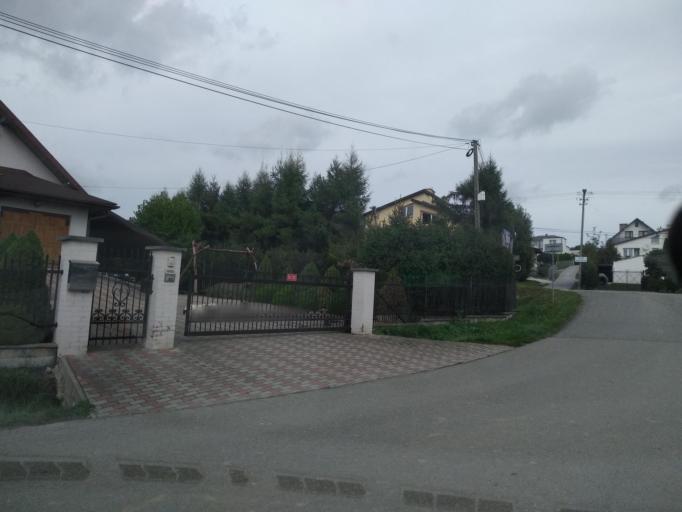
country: PL
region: Lesser Poland Voivodeship
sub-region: Powiat gorlicki
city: Gorlice
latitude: 49.6989
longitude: 21.1557
